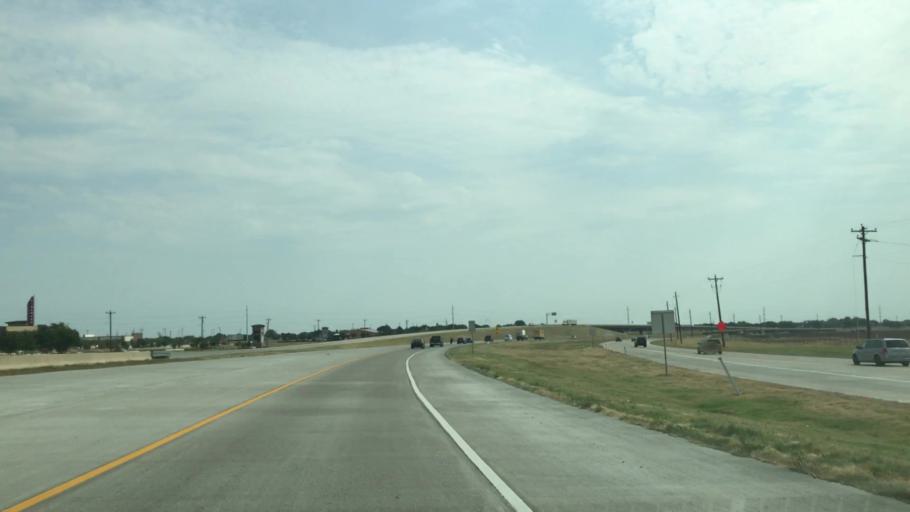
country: US
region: Texas
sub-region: Denton County
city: Roanoke
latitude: 32.9950
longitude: -97.2201
